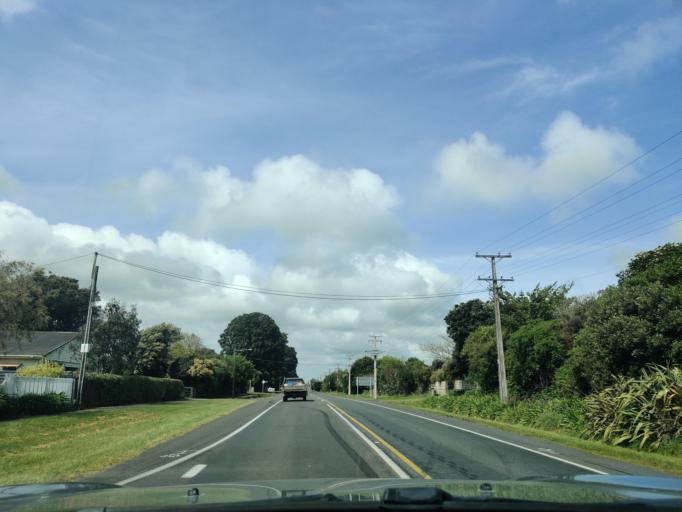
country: NZ
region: Taranaki
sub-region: South Taranaki District
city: Patea
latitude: -39.7649
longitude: 174.6239
